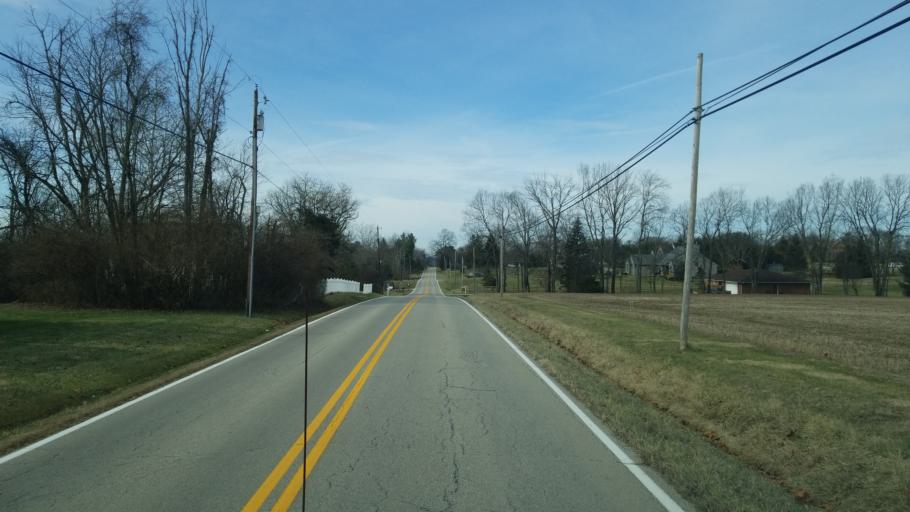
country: US
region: Ohio
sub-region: Warren County
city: Lebanon
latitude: 39.4294
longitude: -84.1485
